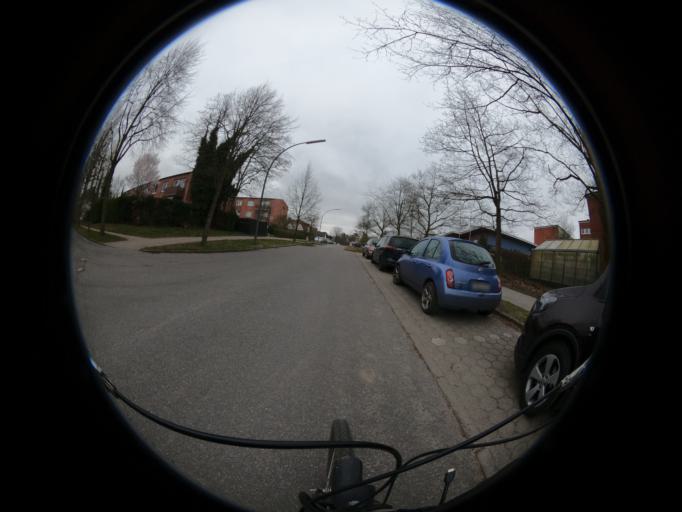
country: DE
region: Lower Saxony
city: Neu Wulmstorf
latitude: 53.4672
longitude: 9.8381
